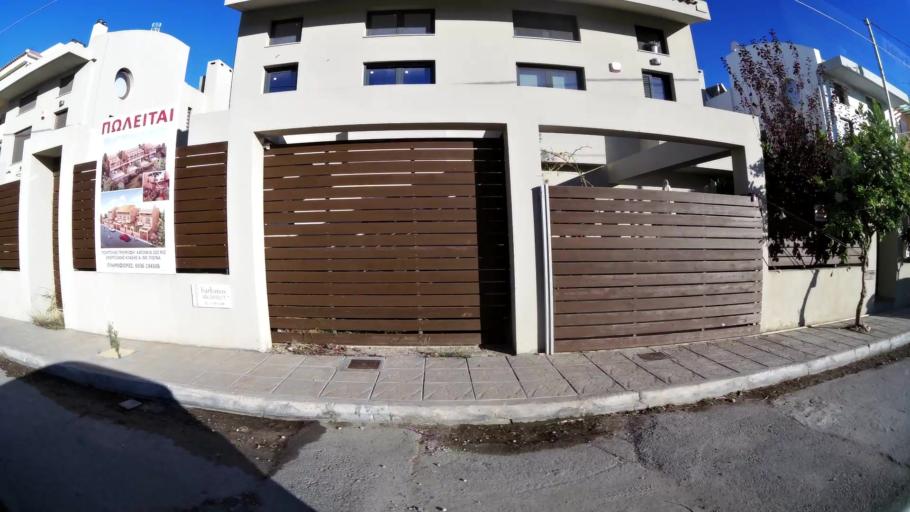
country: GR
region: Attica
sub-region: Nomarchia Anatolikis Attikis
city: Vari
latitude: 37.8232
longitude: 23.8078
